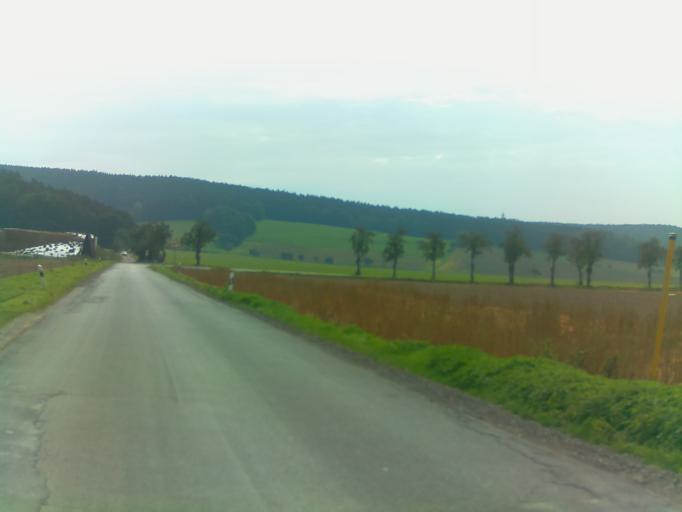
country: DE
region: Thuringia
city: Schops
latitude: 50.8399
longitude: 11.6113
